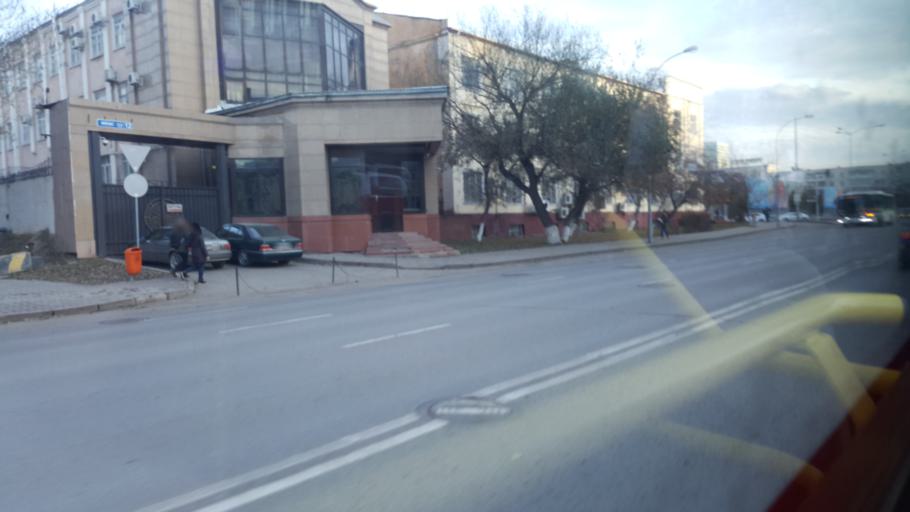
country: KZ
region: Astana Qalasy
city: Astana
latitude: 51.1678
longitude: 71.4135
